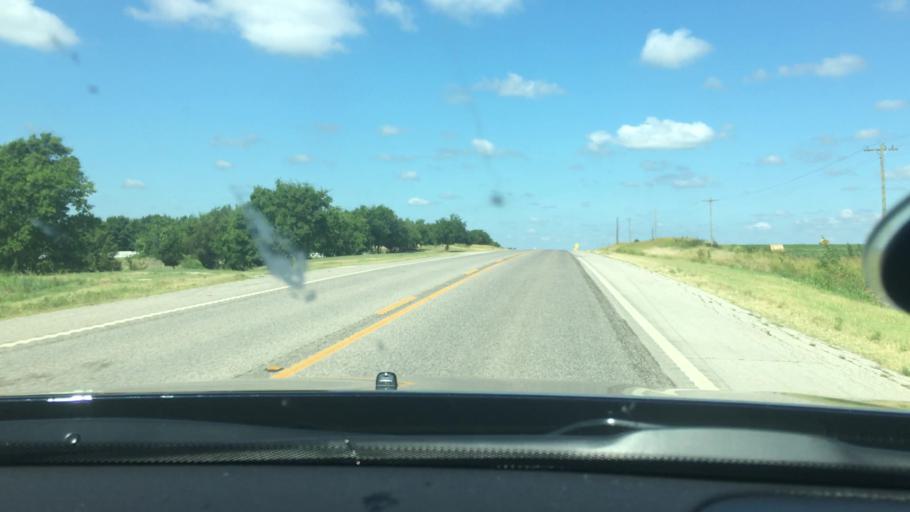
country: US
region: Oklahoma
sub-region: Marshall County
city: Oakland
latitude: 34.0999
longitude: -96.8807
